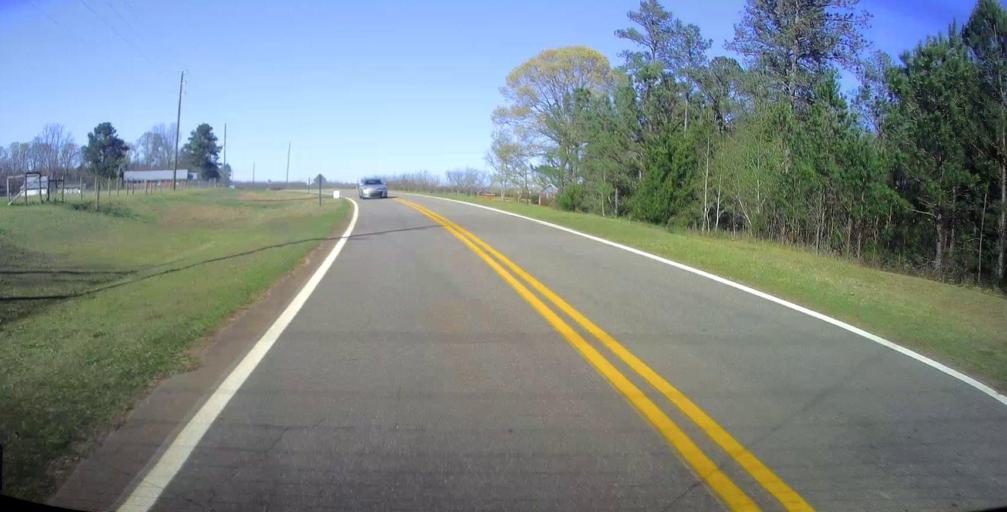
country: US
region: Georgia
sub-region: Peach County
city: Fort Valley
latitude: 32.6022
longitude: -83.9827
